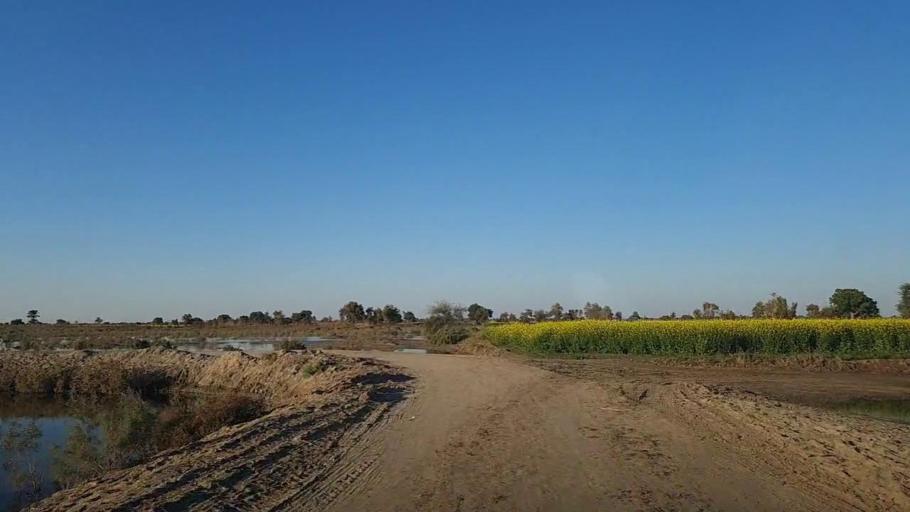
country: PK
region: Sindh
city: Sanghar
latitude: 26.1477
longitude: 68.9265
